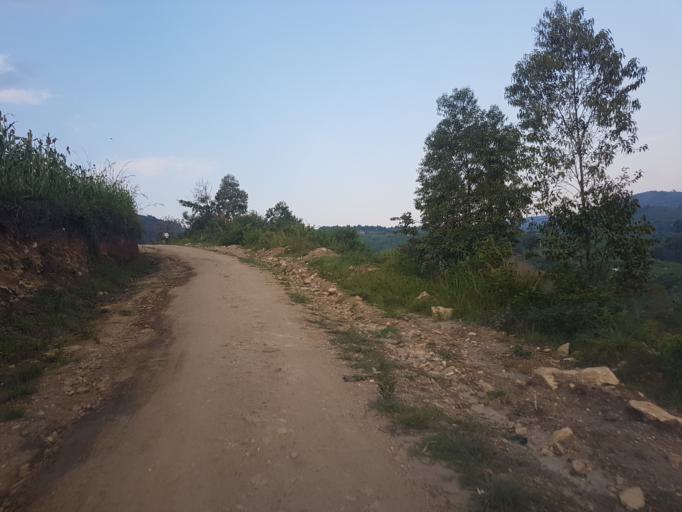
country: UG
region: Western Region
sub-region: Mitoma District
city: Mitoma
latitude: -0.6821
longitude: 29.9105
